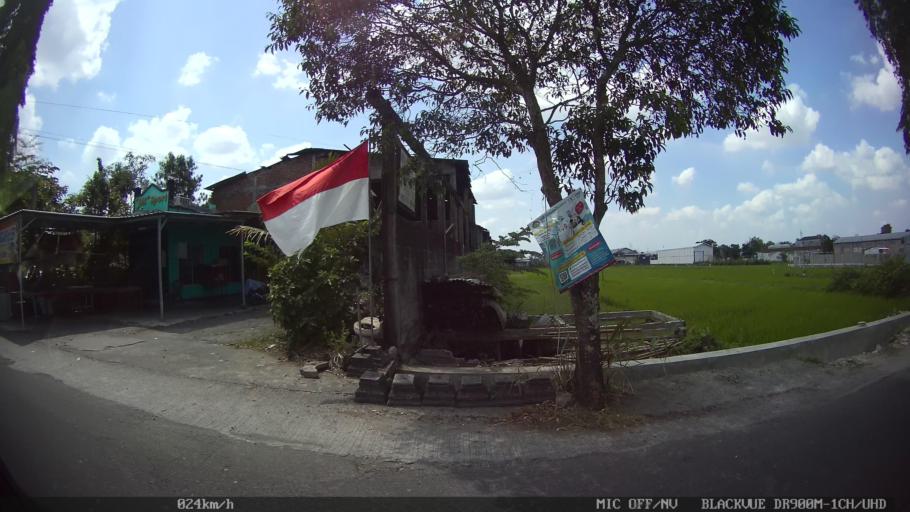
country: ID
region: Daerah Istimewa Yogyakarta
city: Kasihan
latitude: -7.8247
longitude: 110.3453
